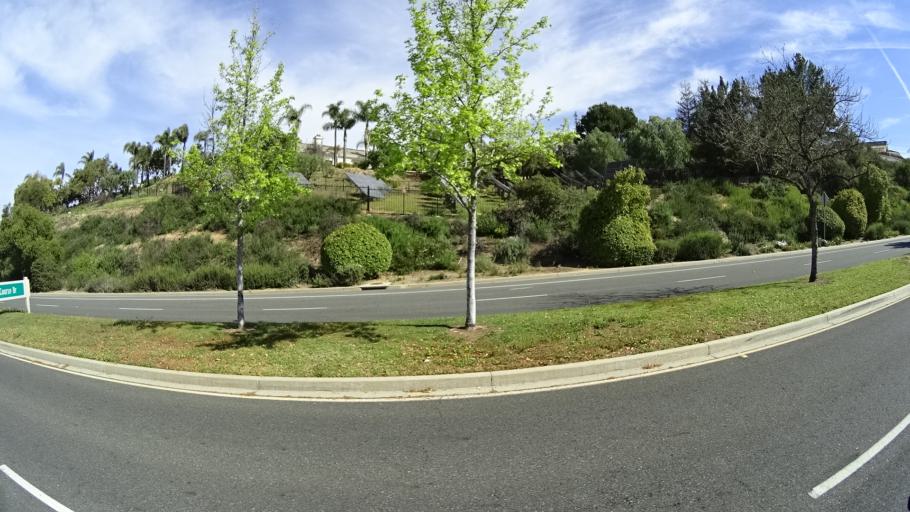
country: US
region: California
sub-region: Ventura County
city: Thousand Oaks
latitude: 34.1961
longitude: -118.8078
